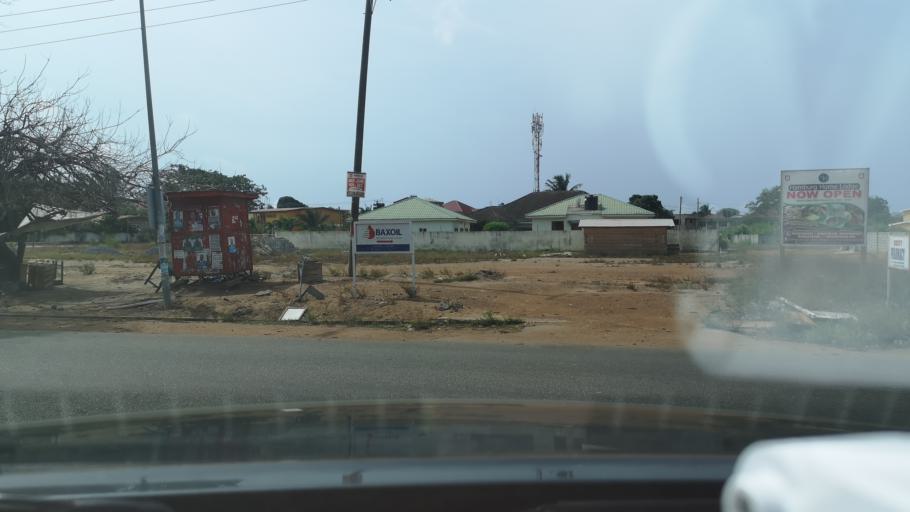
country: GH
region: Greater Accra
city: Tema
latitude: 5.6544
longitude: -0.0221
